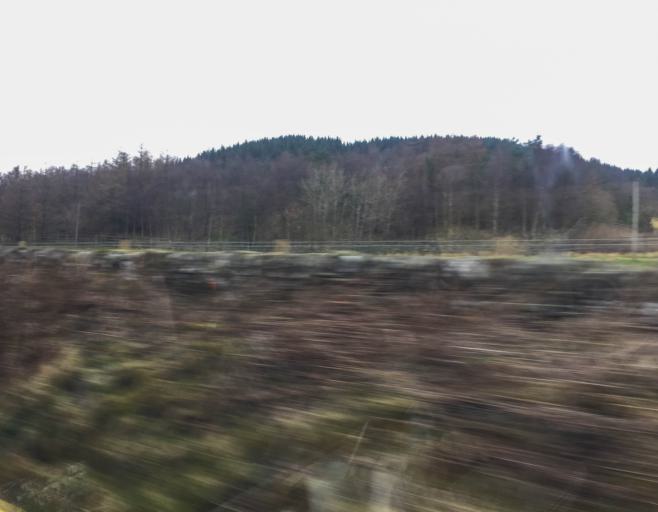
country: GB
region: Scotland
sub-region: Dumfries and Galloway
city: Moffat
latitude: 55.4264
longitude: -3.6076
